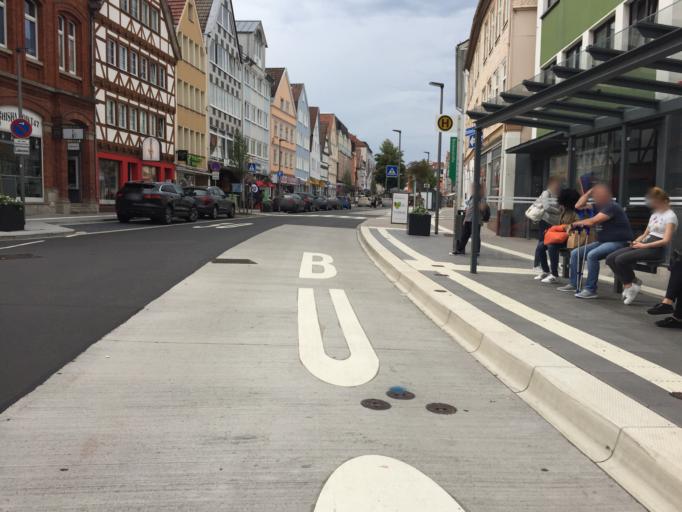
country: DE
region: Hesse
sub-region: Regierungsbezirk Kassel
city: Bad Hersfeld
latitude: 50.8670
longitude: 9.7114
